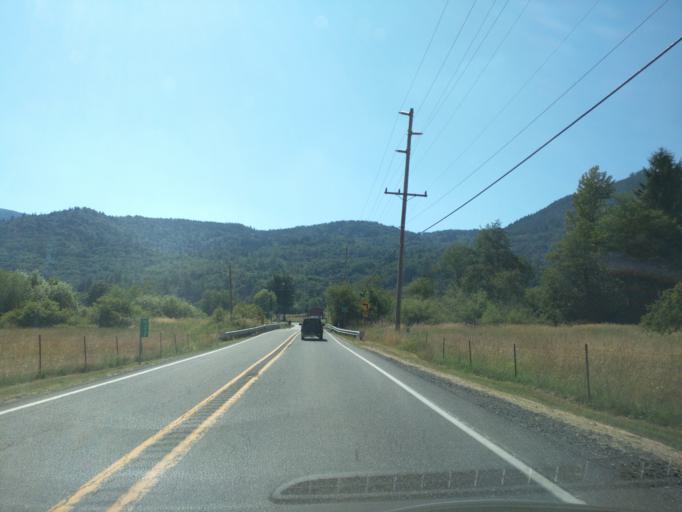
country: US
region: Washington
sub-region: Whatcom County
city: Peaceful Valley
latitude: 48.9051
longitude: -122.1399
